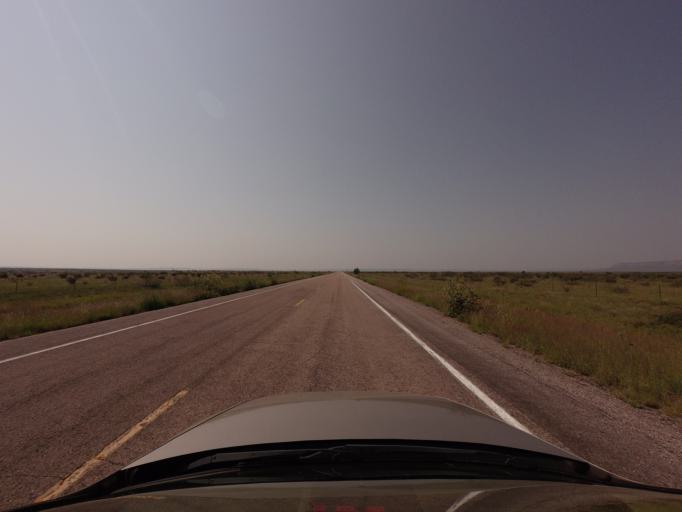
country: US
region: New Mexico
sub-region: Quay County
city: Tucumcari
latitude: 34.9716
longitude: -103.7529
